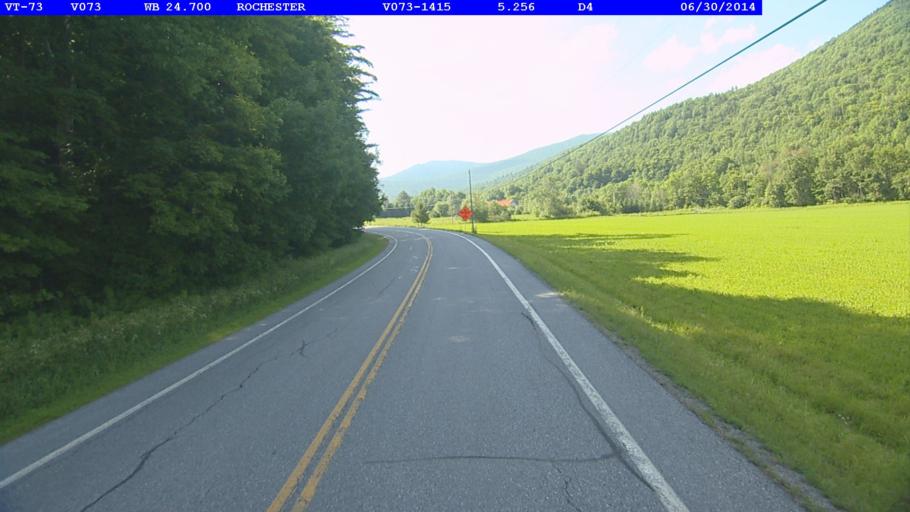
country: US
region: Vermont
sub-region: Orange County
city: Randolph
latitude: 43.8561
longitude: -72.8671
